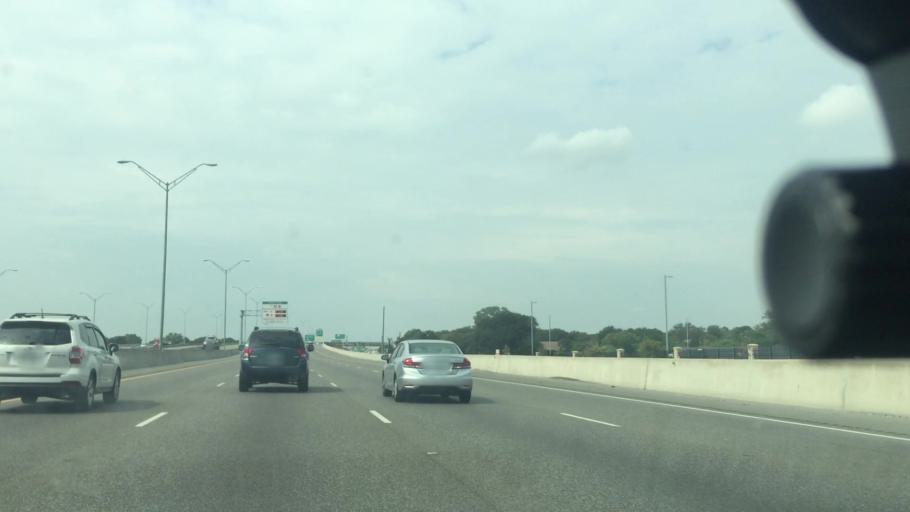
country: US
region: Texas
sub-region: Tarrant County
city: Hurst
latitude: 32.8403
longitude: -97.1626
